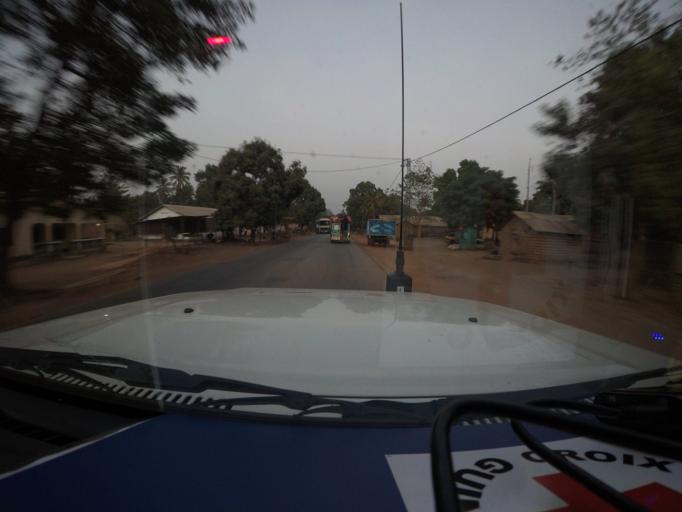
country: GN
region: Kindia
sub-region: Kindia
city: Kindia
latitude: 9.9498
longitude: -12.9511
